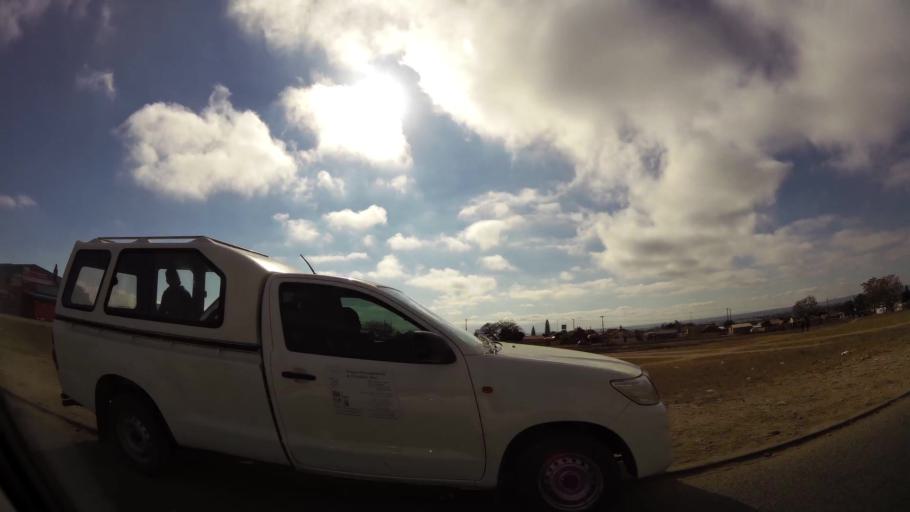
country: ZA
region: Limpopo
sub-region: Capricorn District Municipality
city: Polokwane
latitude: -23.8520
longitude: 29.3830
